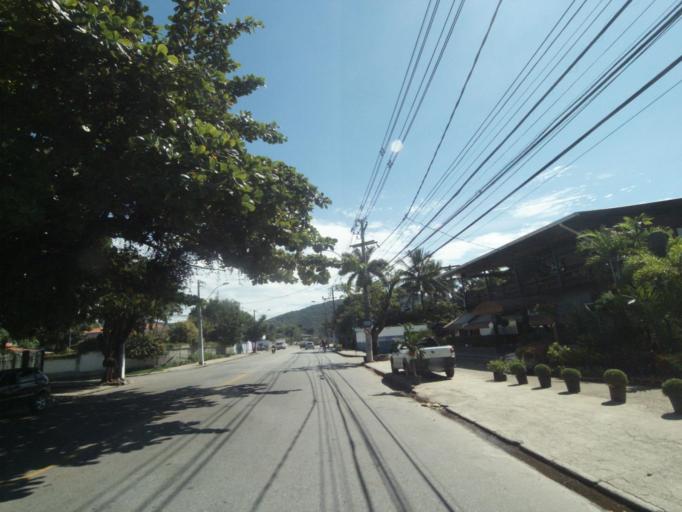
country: BR
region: Rio de Janeiro
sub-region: Niteroi
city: Niteroi
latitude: -22.9483
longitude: -43.0576
